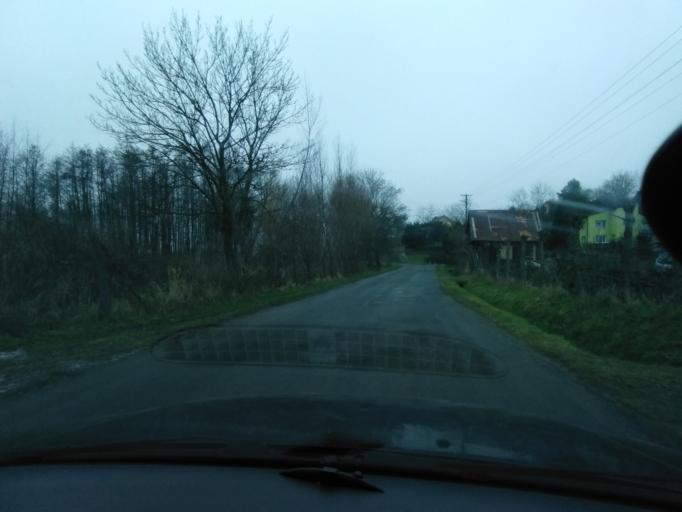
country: PL
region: Subcarpathian Voivodeship
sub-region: Powiat przeworski
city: Zarzecze
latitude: 49.9662
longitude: 22.5669
